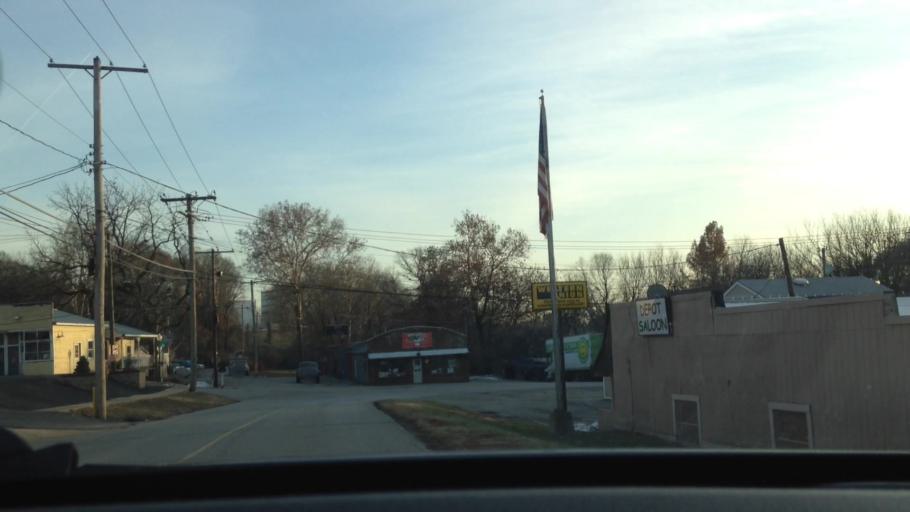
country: US
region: Missouri
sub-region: Clay County
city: North Kansas City
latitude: 39.1549
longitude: -94.5474
